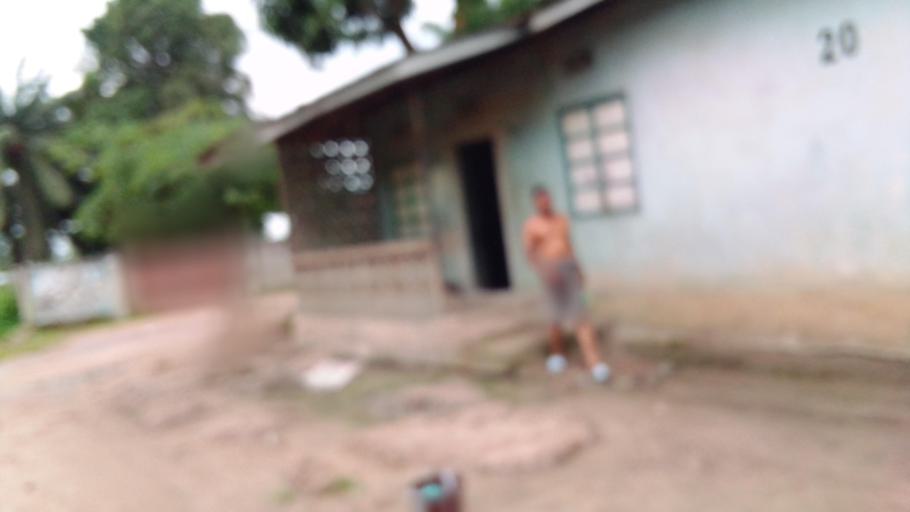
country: SL
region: Eastern Province
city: Kenema
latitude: 7.8572
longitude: -11.1994
